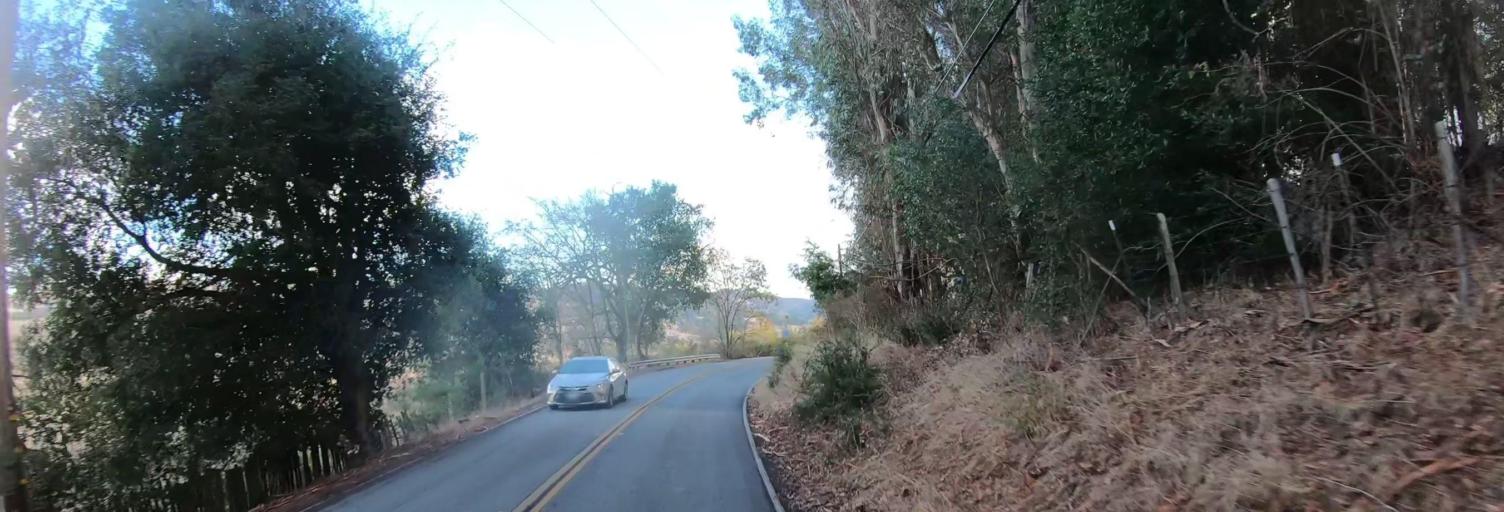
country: US
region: California
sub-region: Santa Clara County
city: East Foothills
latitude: 37.3427
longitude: -121.7227
